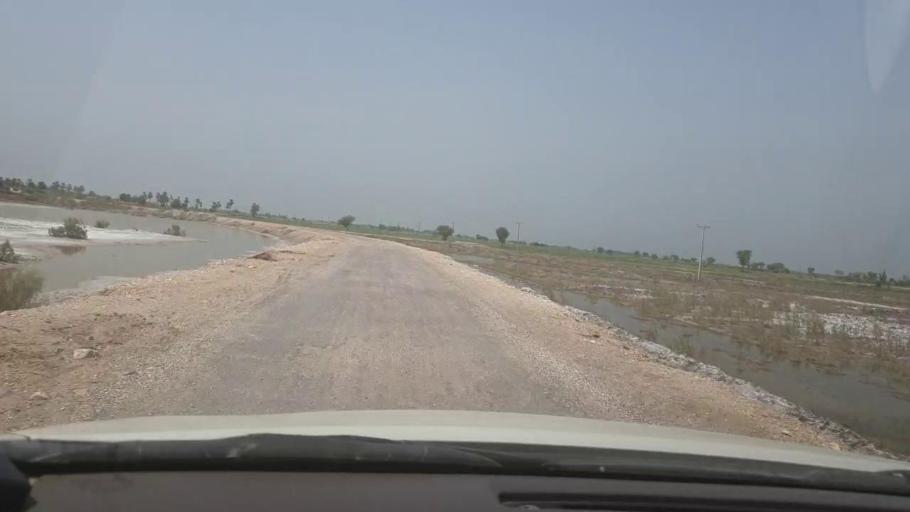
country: PK
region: Sindh
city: Garhi Yasin
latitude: 27.9758
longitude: 68.5476
